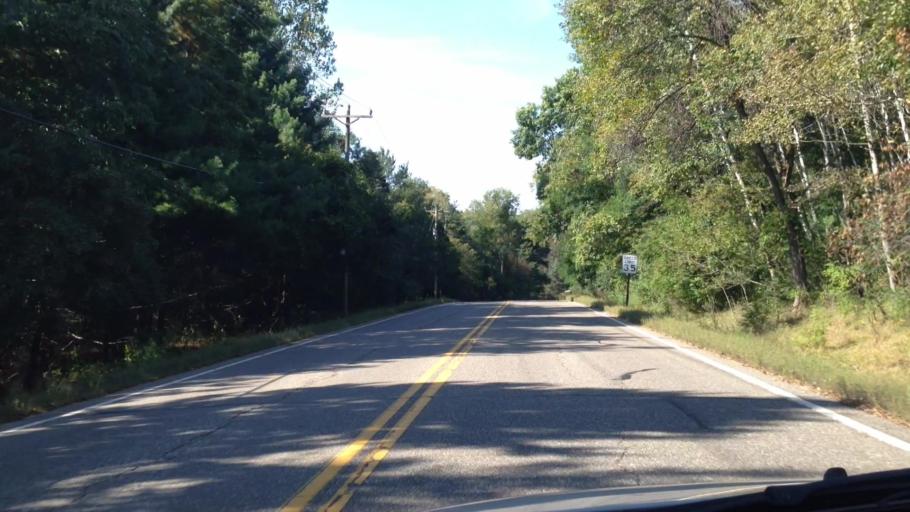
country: US
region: Minnesota
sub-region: Washington County
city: Stillwater
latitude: 45.0818
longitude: -92.8115
